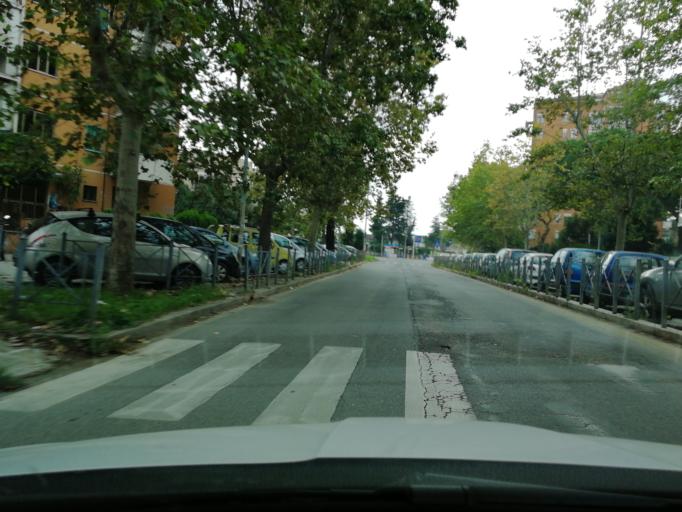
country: IT
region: Latium
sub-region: Citta metropolitana di Roma Capitale
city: Rome
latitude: 41.8571
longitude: 12.5536
